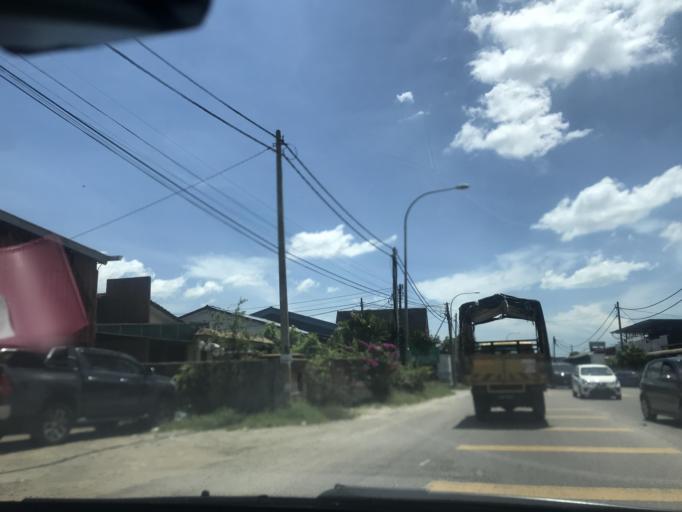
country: MY
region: Kelantan
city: Kota Bharu
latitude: 6.1164
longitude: 102.2687
